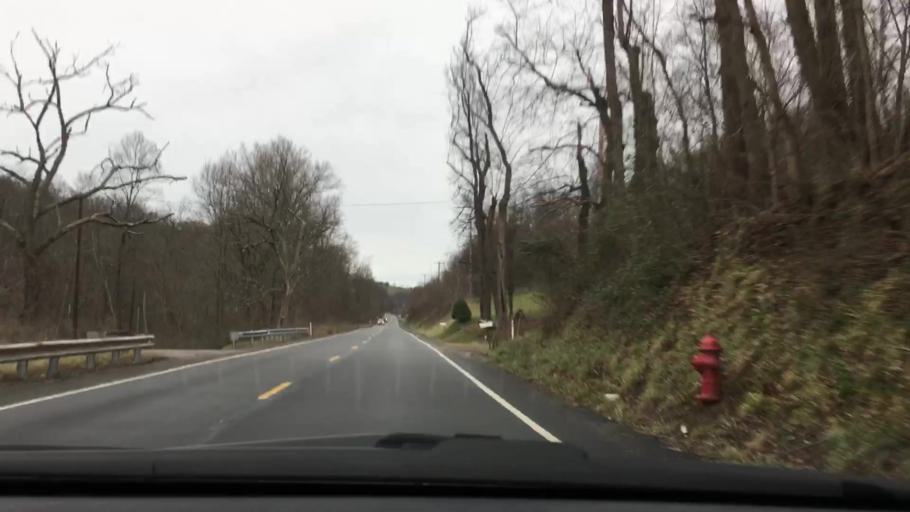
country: US
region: Pennsylvania
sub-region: Greene County
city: Morrisville
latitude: 39.8806
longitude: -80.1620
